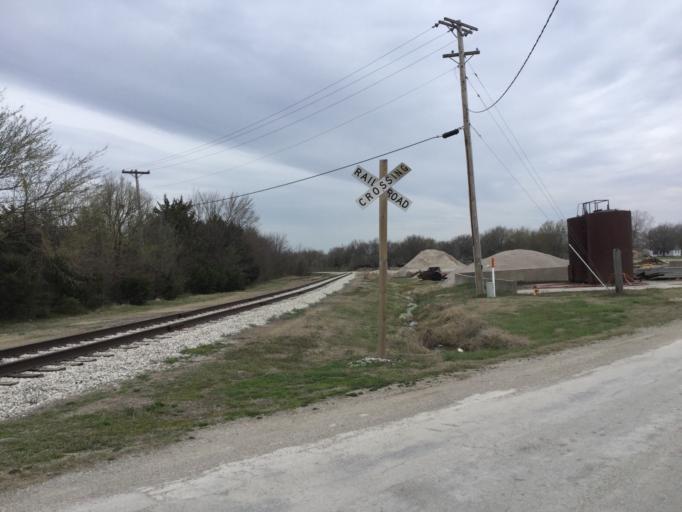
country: US
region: Kansas
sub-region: Wilson County
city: Fredonia
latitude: 37.5425
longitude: -95.8283
